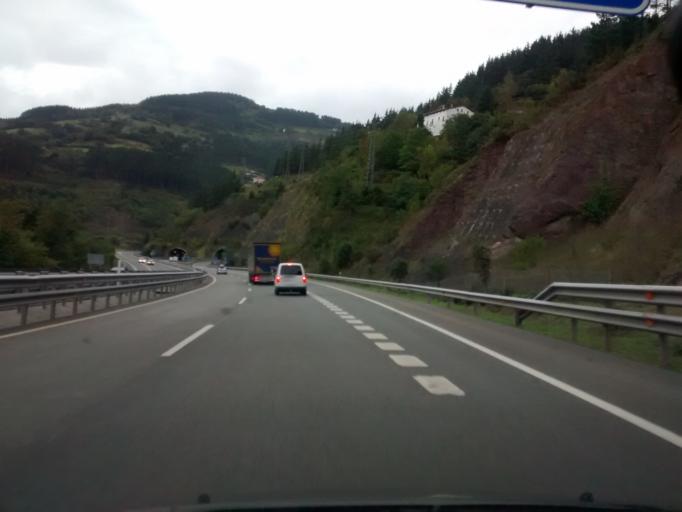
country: ES
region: Basque Country
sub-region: Provincia de Guipuzcoa
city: Elgoibar
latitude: 43.1903
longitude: -2.4303
